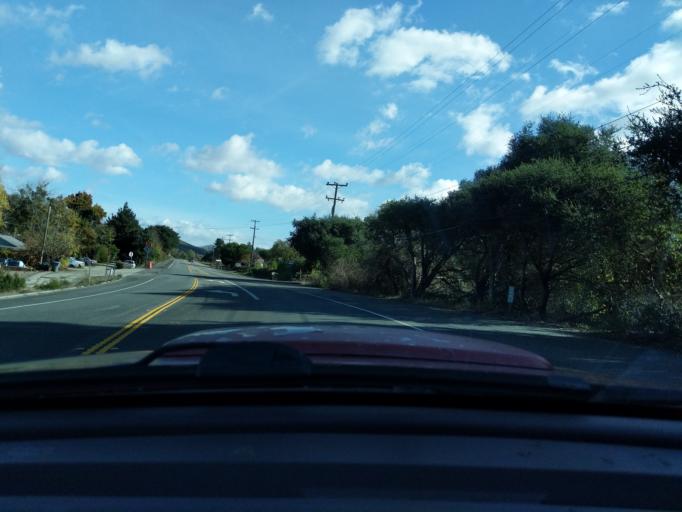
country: US
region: California
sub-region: San Benito County
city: Aromas
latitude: 36.8997
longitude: -121.5955
